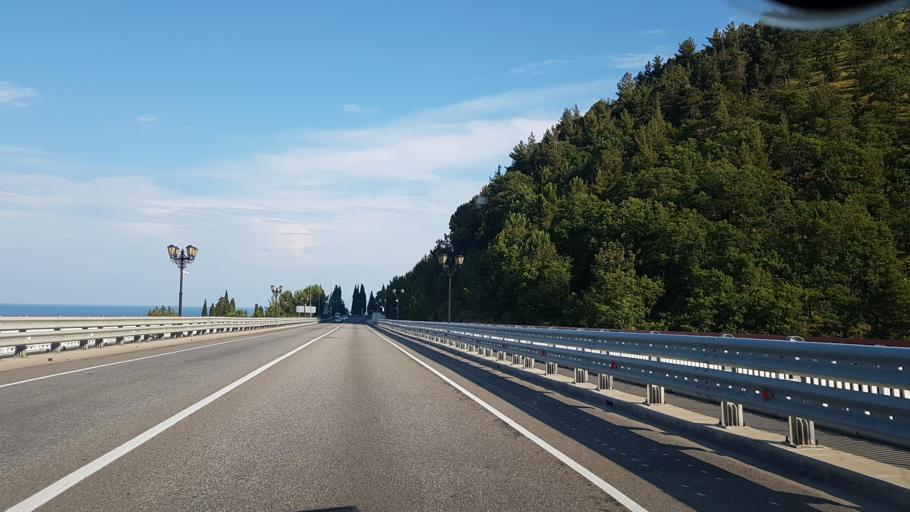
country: RU
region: Krasnodarskiy
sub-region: Sochi City
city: Lazarevskoye
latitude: 43.8305
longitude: 39.4249
